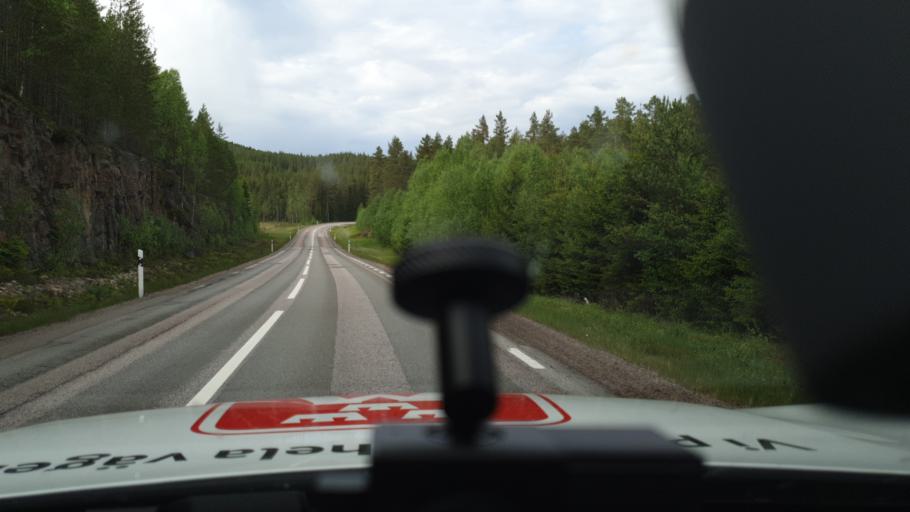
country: SE
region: Vaermland
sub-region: Torsby Kommun
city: Torsby
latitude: 60.3076
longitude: 13.0951
